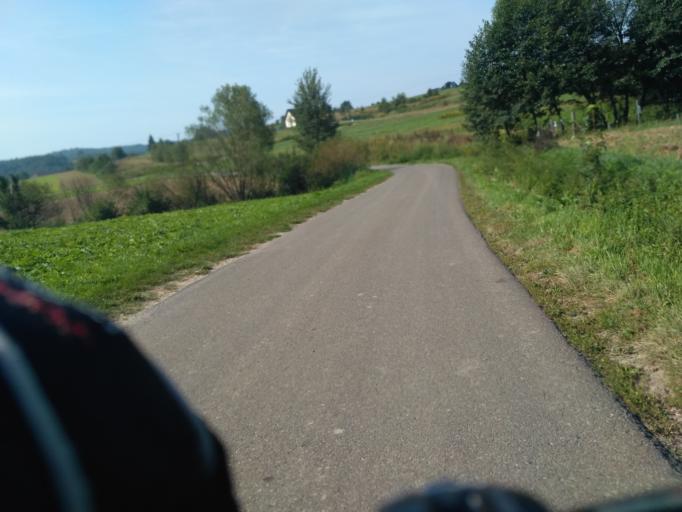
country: PL
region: Subcarpathian Voivodeship
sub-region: Powiat brzozowski
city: Golcowa
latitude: 49.7816
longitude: 22.0140
